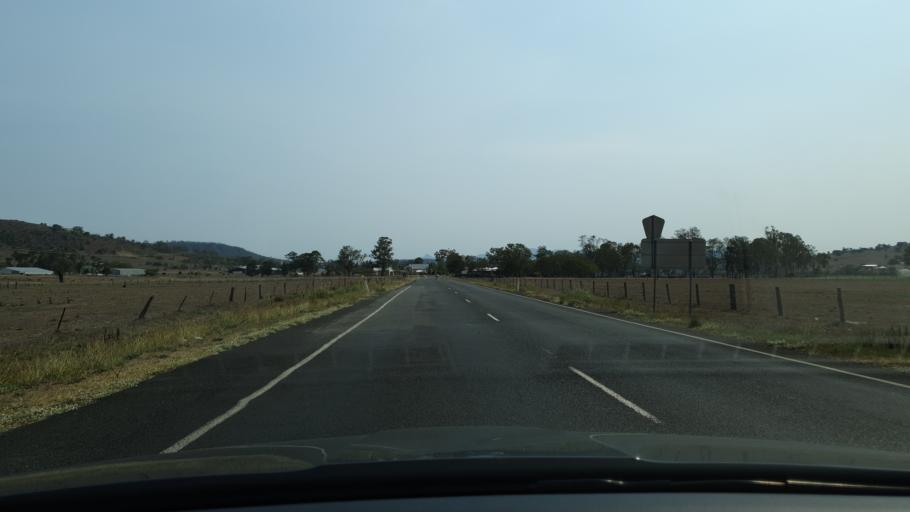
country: AU
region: Queensland
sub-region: Ipswich
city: Deebing Heights
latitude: -28.0093
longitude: 152.6789
